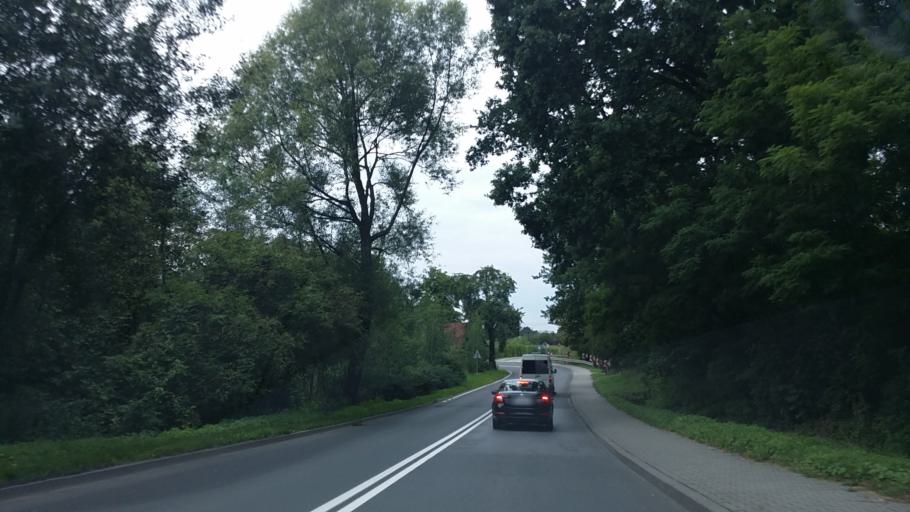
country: PL
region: Lesser Poland Voivodeship
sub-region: Powiat wadowicki
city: Ryczow
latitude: 49.9860
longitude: 19.5436
